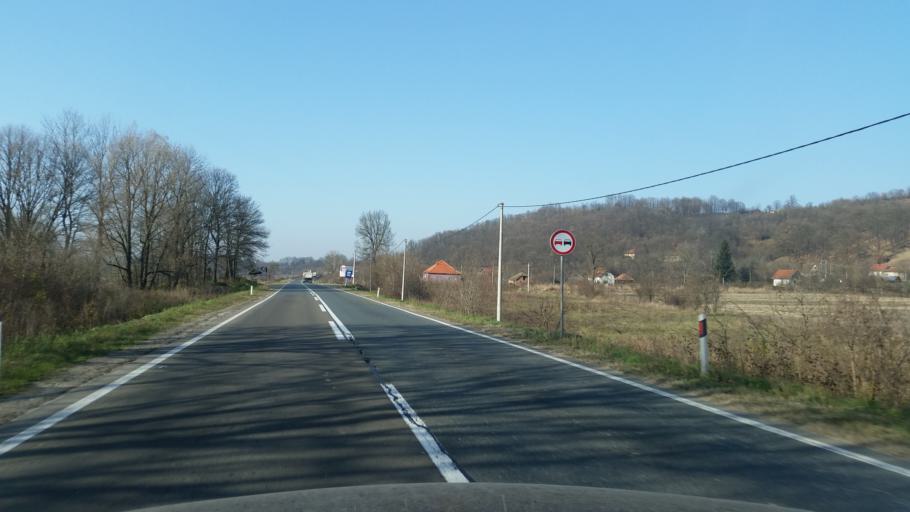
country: RS
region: Central Serbia
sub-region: Kolubarski Okrug
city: Lajkovac
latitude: 44.3420
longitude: 20.2044
